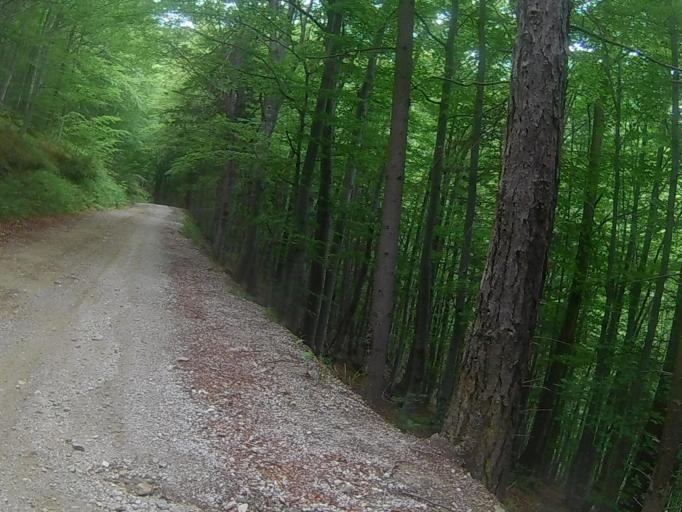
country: SI
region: Maribor
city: Limbus
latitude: 46.5230
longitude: 15.5710
